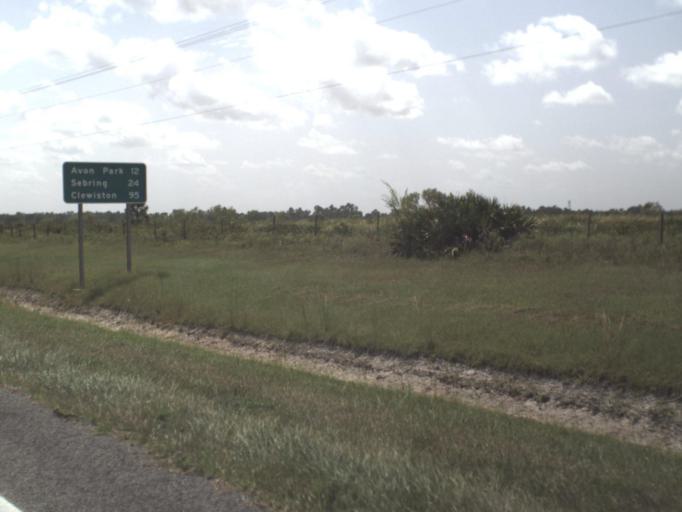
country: US
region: Florida
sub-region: Polk County
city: Frostproof
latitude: 27.7542
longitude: -81.5872
